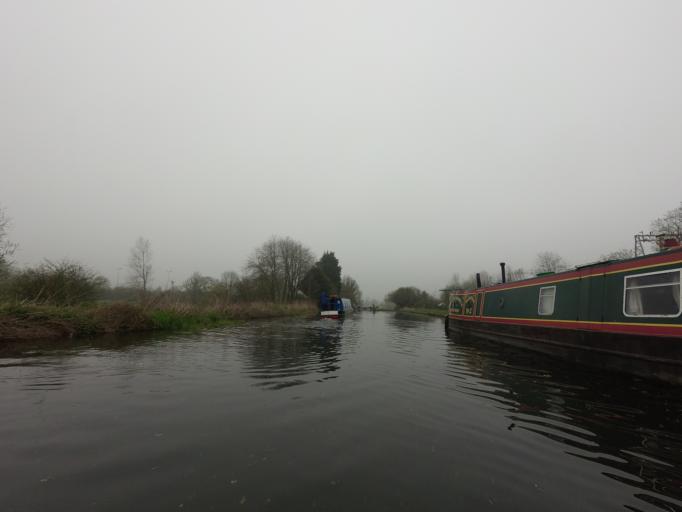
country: GB
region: England
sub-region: Hertfordshire
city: Hemel Hempstead
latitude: 51.7452
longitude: -0.5020
